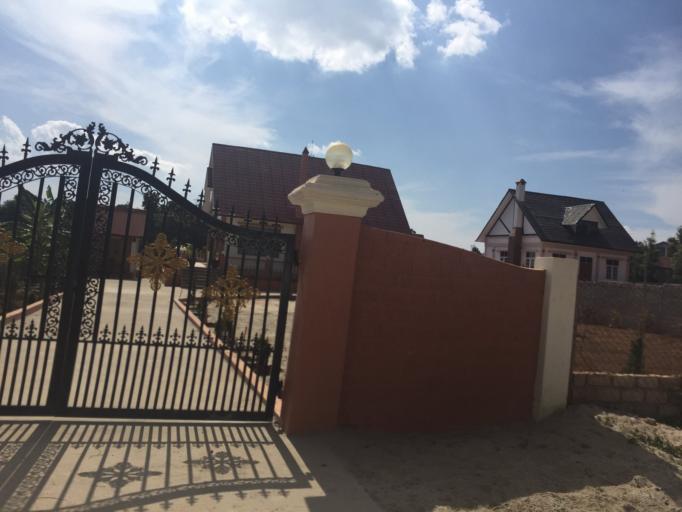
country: MM
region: Mandalay
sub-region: Pyin Oo Lwin District
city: Pyin Oo Lwin
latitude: 22.0832
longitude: 96.5180
